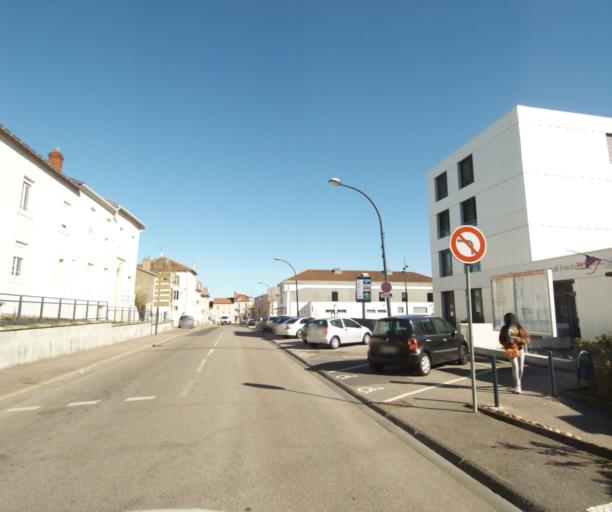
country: FR
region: Lorraine
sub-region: Departement de Meurthe-et-Moselle
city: Jarville-la-Malgrange
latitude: 48.6694
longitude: 6.2046
